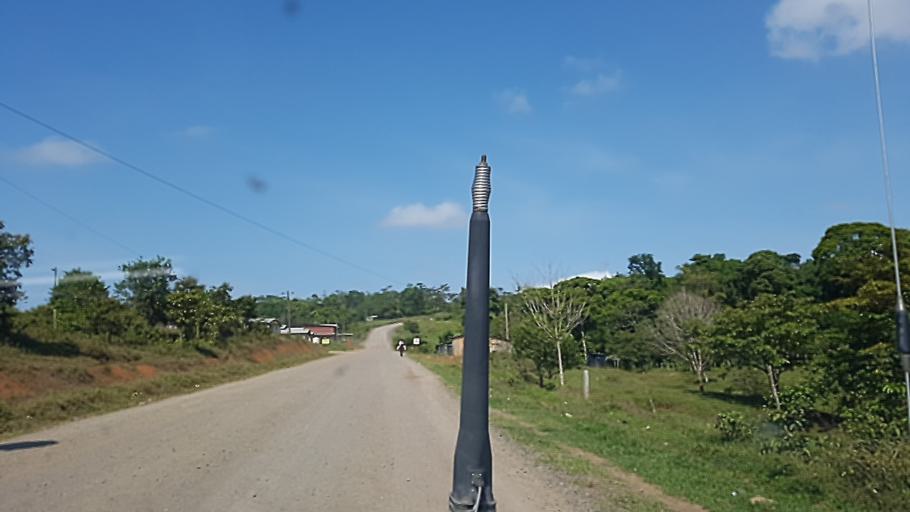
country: NI
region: Atlantico Sur
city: Nueva Guinea
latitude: 11.7899
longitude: -84.1606
